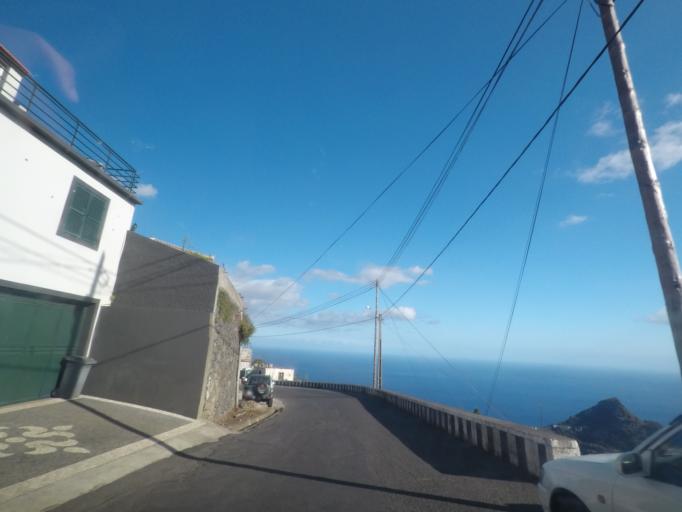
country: PT
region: Madeira
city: Camara de Lobos
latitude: 32.6636
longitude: -16.9937
